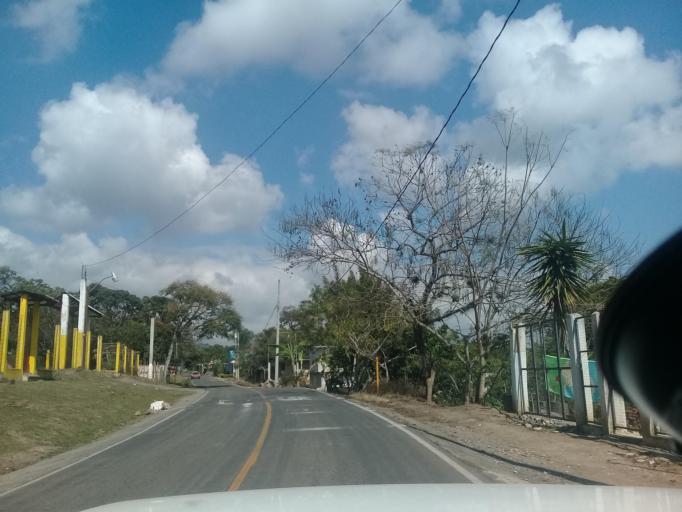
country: MX
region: Veracruz
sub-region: Coatepec
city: Bella Esperanza
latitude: 19.4360
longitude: -96.8681
